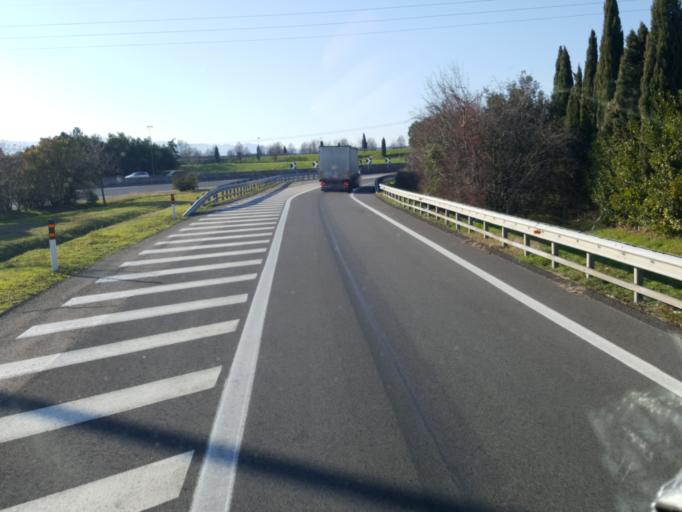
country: IT
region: Tuscany
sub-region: Province of Florence
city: Campi Bisenzio
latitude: 43.8275
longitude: 11.1616
